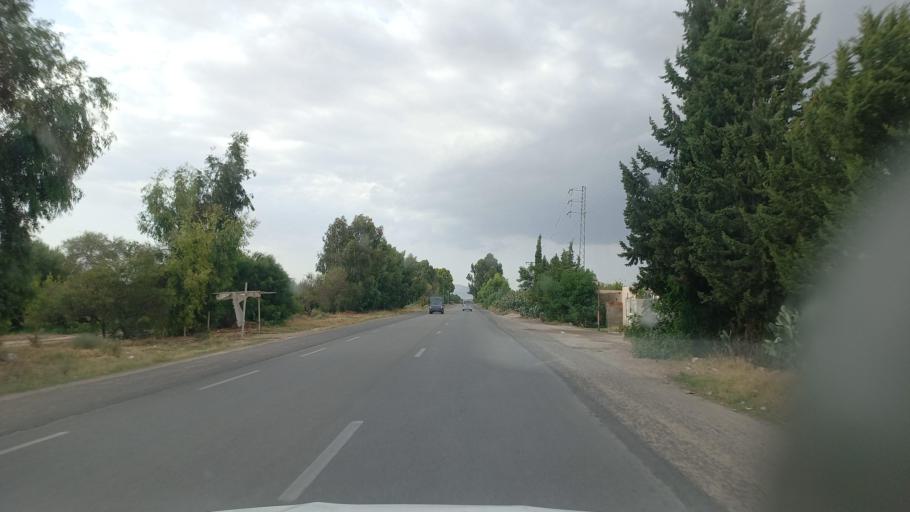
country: TN
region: Al Qasrayn
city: Sbiba
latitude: 35.2959
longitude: 9.0899
